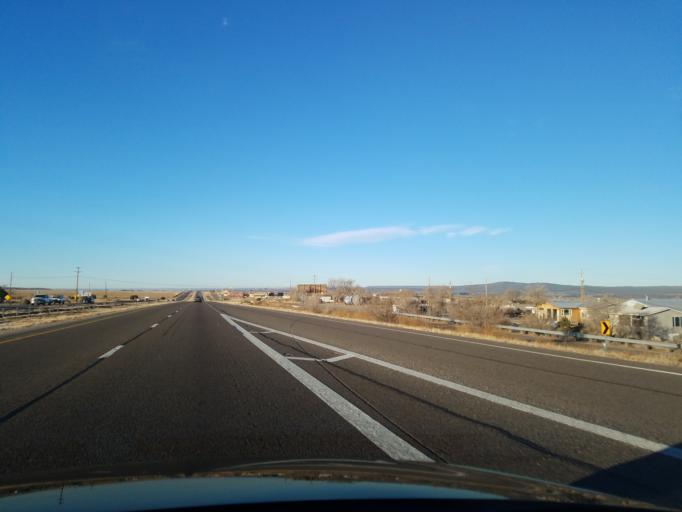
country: US
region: New Mexico
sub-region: Sandoval County
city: Santo Domingo Pueblo
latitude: 35.4580
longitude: -106.3348
